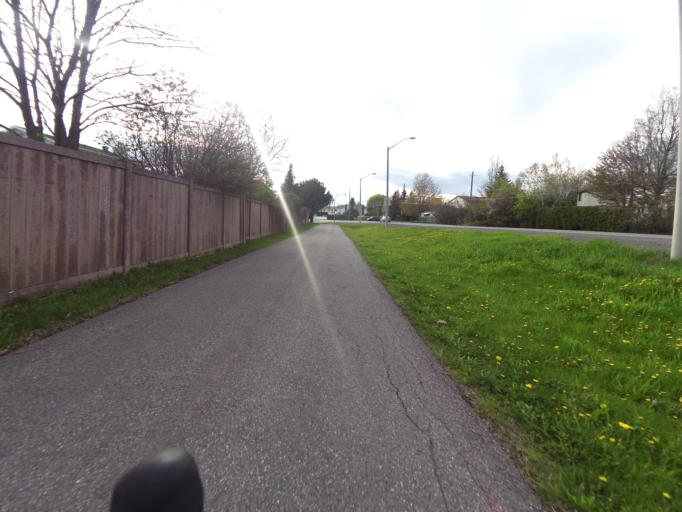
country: CA
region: Ontario
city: Bells Corners
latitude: 45.2758
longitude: -75.7707
